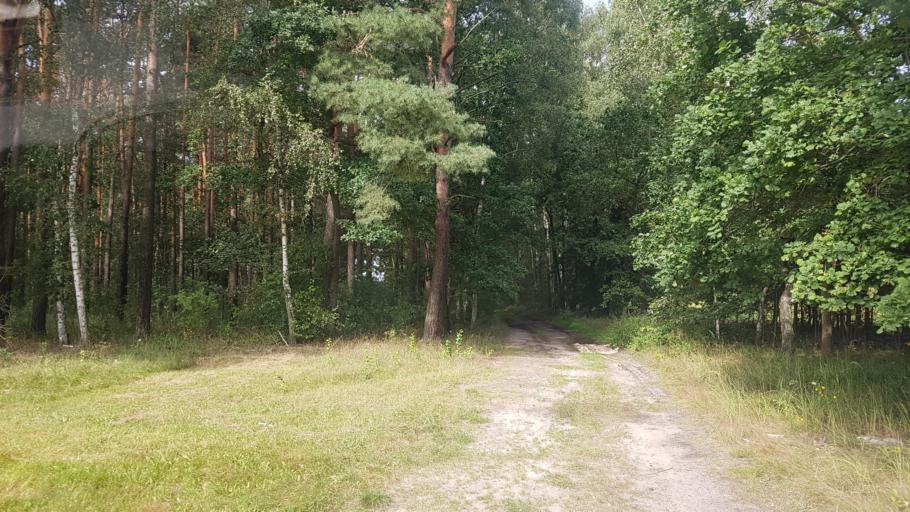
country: DE
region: Brandenburg
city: Bronkow
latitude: 51.6336
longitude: 13.8840
